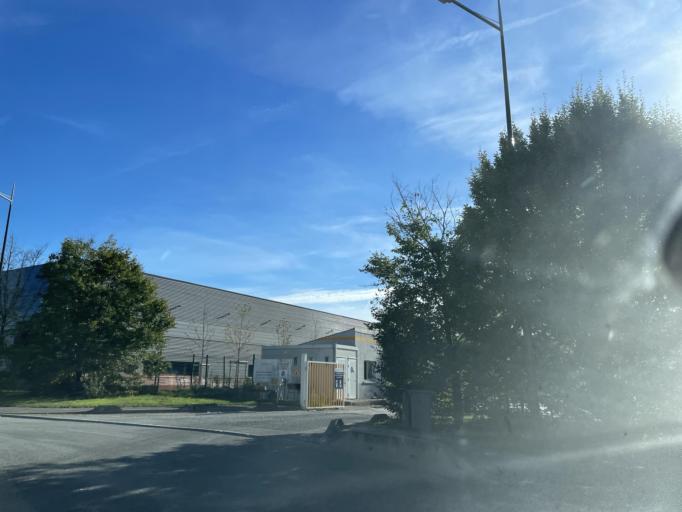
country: FR
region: Ile-de-France
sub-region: Departement du Val-de-Marne
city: Bonneuil-sur-Marne
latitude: 48.7806
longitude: 2.4833
